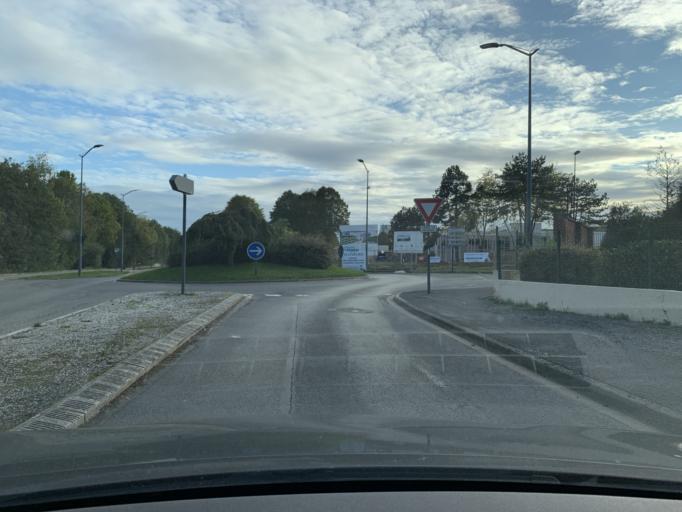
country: FR
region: Picardie
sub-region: Departement de l'Aisne
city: Harly
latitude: 49.8546
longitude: 3.3104
